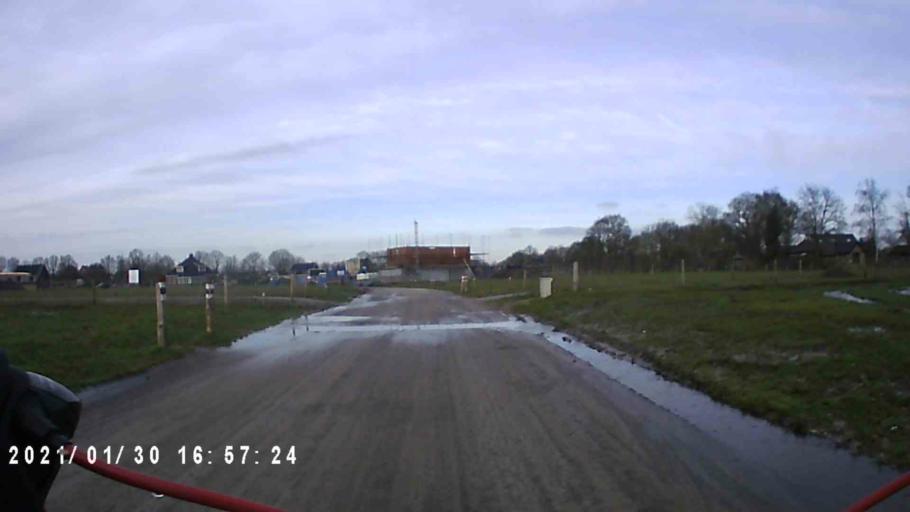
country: NL
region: Groningen
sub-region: Gemeente Leek
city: Leek
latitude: 53.1504
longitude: 6.3800
